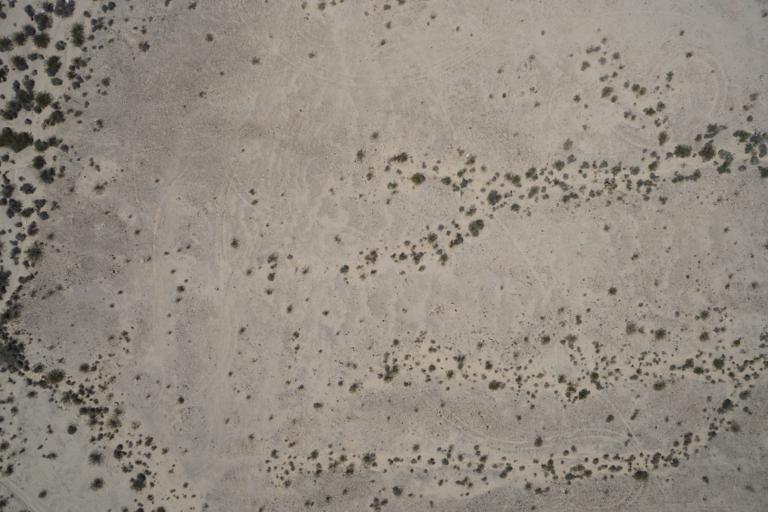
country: US
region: California
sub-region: San Bernardino County
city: Twentynine Palms
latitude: 34.1342
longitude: -116.0316
